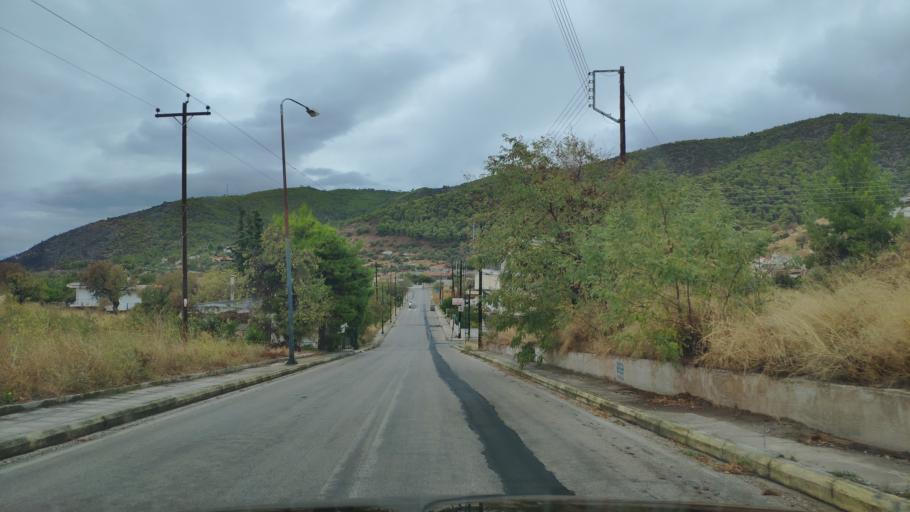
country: GR
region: Peloponnese
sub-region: Nomos Korinthias
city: Perachora
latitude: 38.0273
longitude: 22.9475
